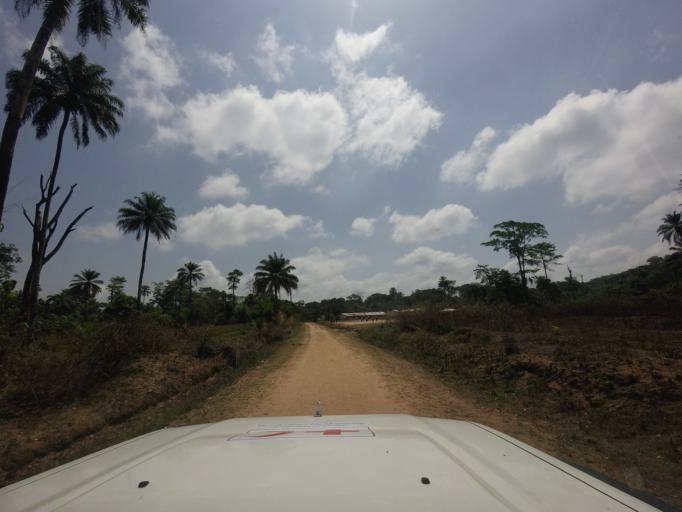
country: LR
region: Lofa
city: Voinjama
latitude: 8.4868
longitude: -9.6600
